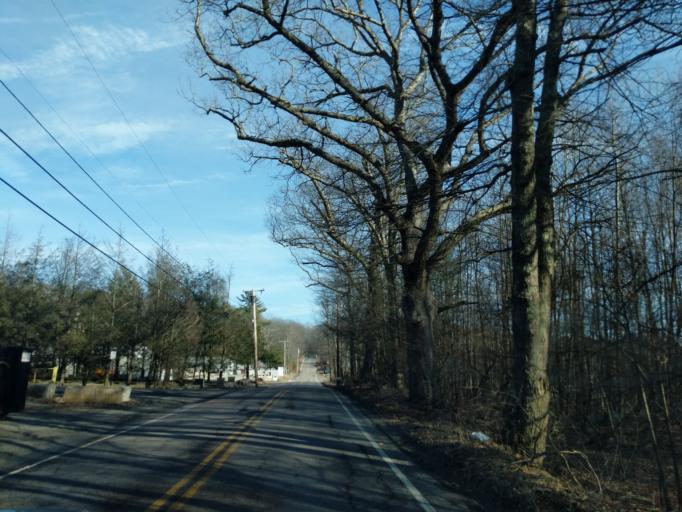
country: US
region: Massachusetts
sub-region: Worcester County
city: Millville
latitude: 42.0273
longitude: -71.5672
